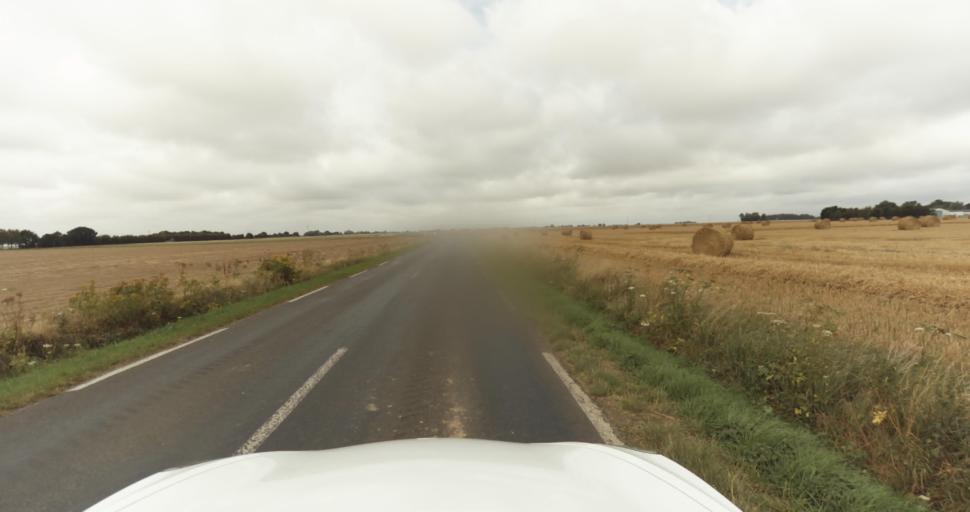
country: FR
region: Haute-Normandie
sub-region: Departement de l'Eure
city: Claville
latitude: 49.0747
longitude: 1.0640
